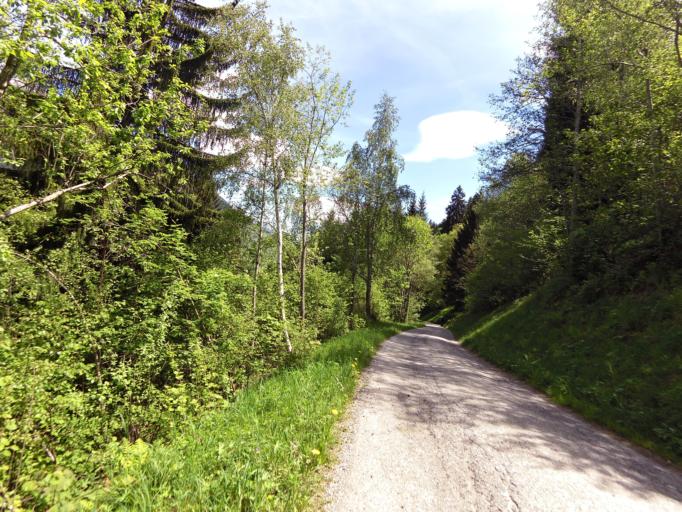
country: CH
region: Grisons
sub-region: Surselva District
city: Disentis
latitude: 46.7129
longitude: 8.8923
